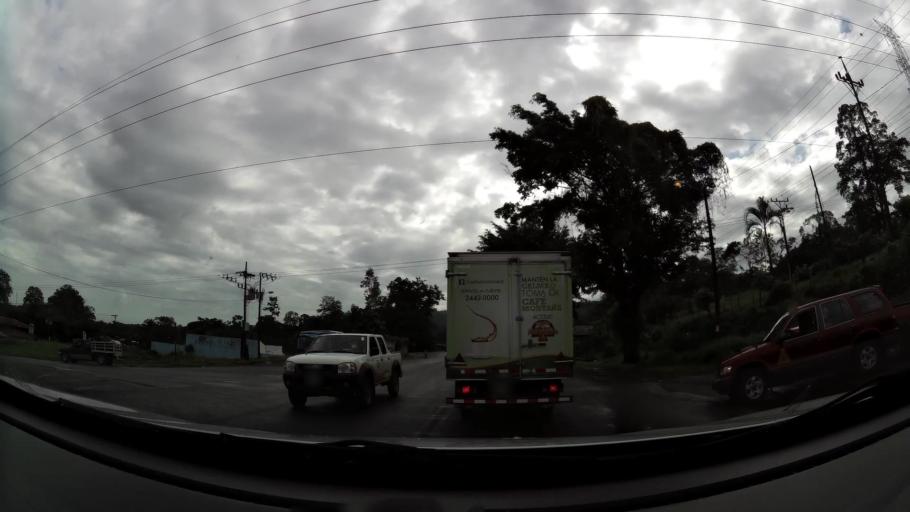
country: CR
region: Limon
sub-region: Canton de Siquirres
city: Siquirres
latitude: 10.0932
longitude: -83.5077
